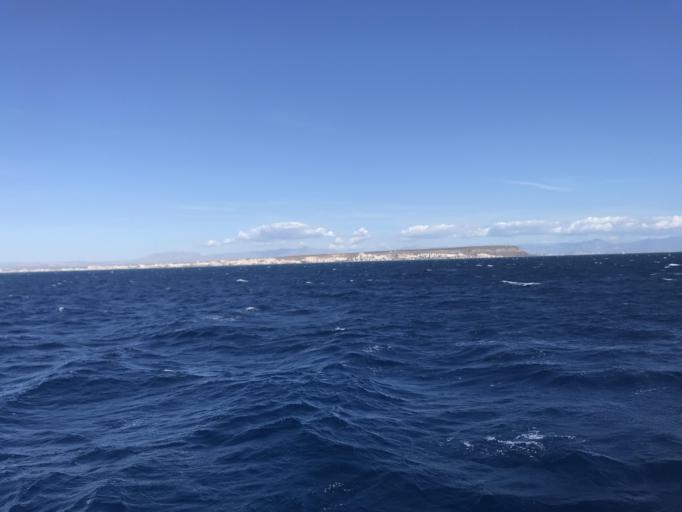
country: ES
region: Valencia
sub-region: Provincia de Alicante
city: Santa Pola
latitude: 38.1421
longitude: -0.5237
